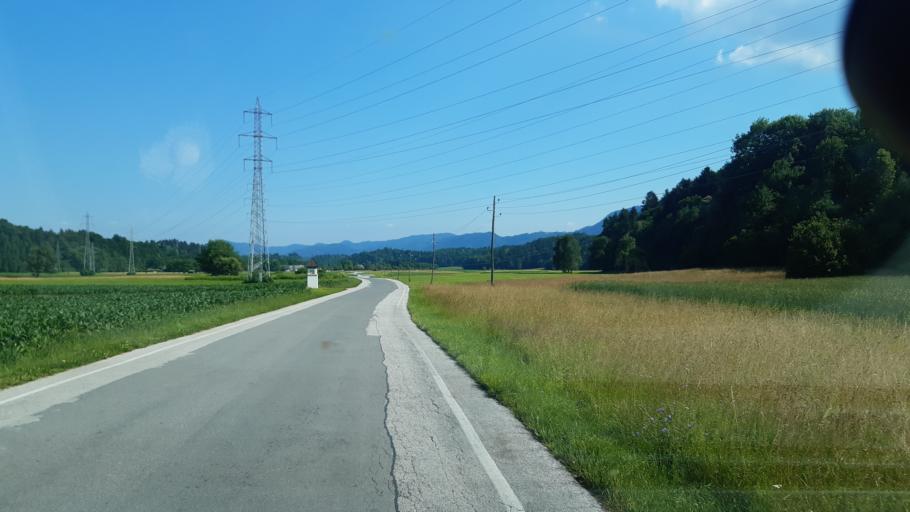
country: SI
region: Radovljica
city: Radovljica
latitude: 46.3573
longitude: 14.1986
